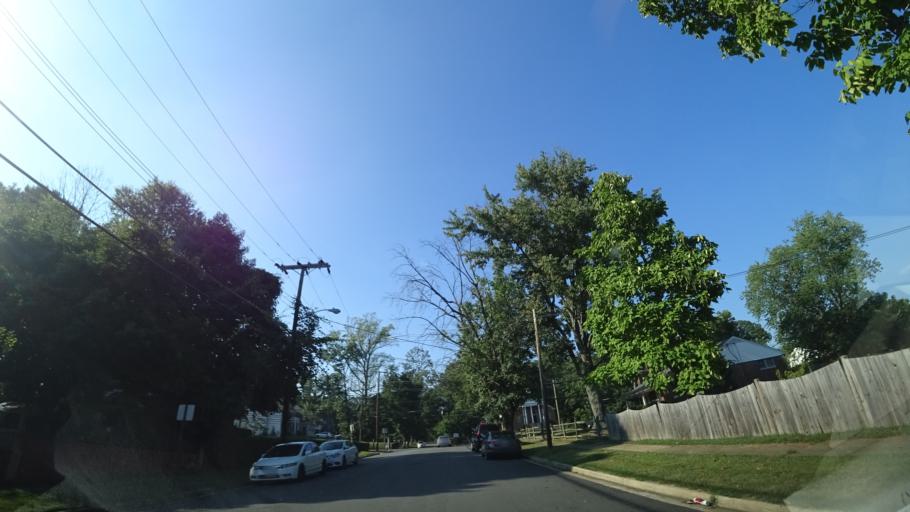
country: US
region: Virginia
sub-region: Fairfax County
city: Springfield
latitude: 38.8112
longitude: -77.1779
